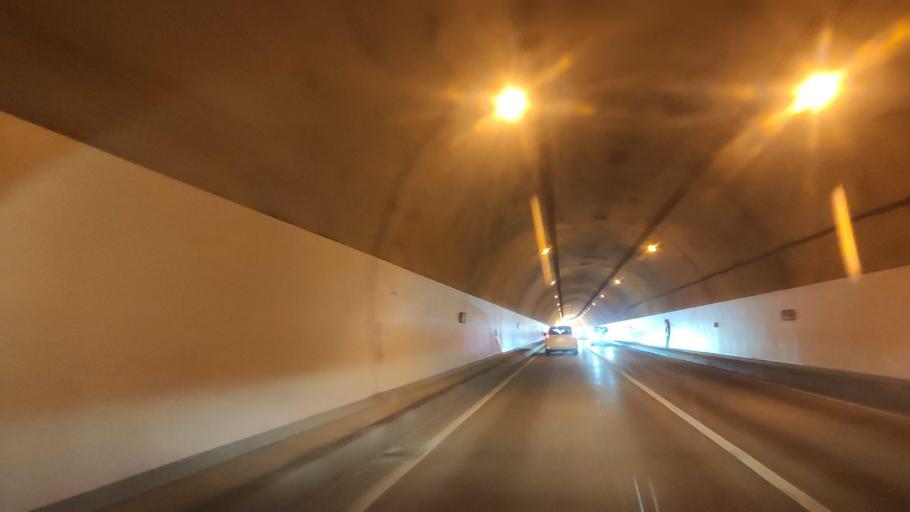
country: JP
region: Hokkaido
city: Ishikari
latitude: 43.4735
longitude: 141.3956
